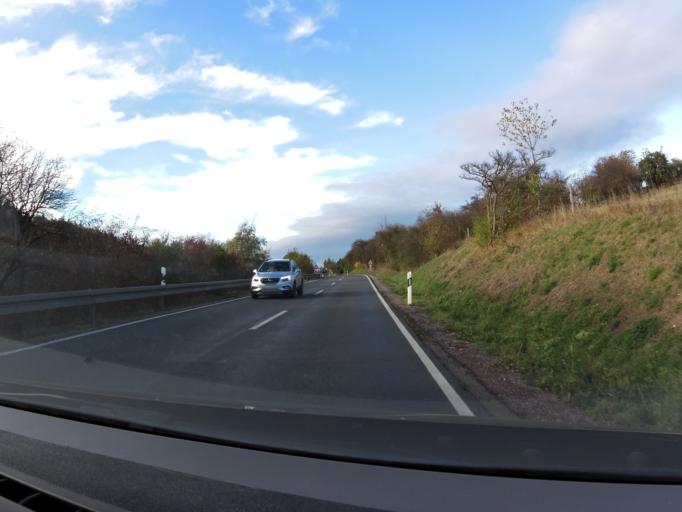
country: DE
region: Thuringia
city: Grafenroda
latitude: 50.7523
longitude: 10.7937
